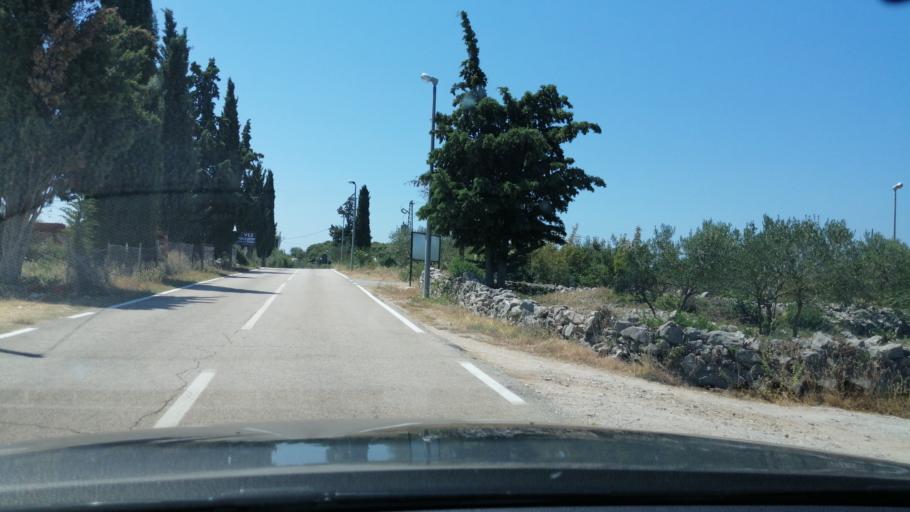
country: HR
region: Sibensko-Kniniska
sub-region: Grad Sibenik
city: Pirovac
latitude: 43.8267
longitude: 15.6784
